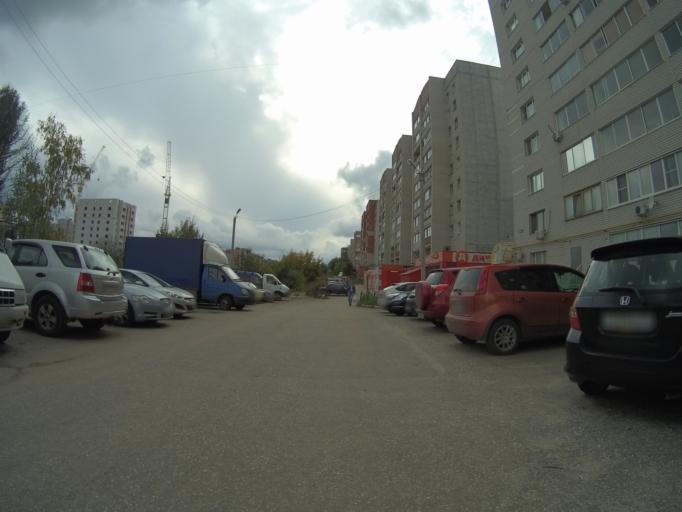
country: RU
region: Vladimir
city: Vladimir
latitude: 56.1114
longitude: 40.3574
